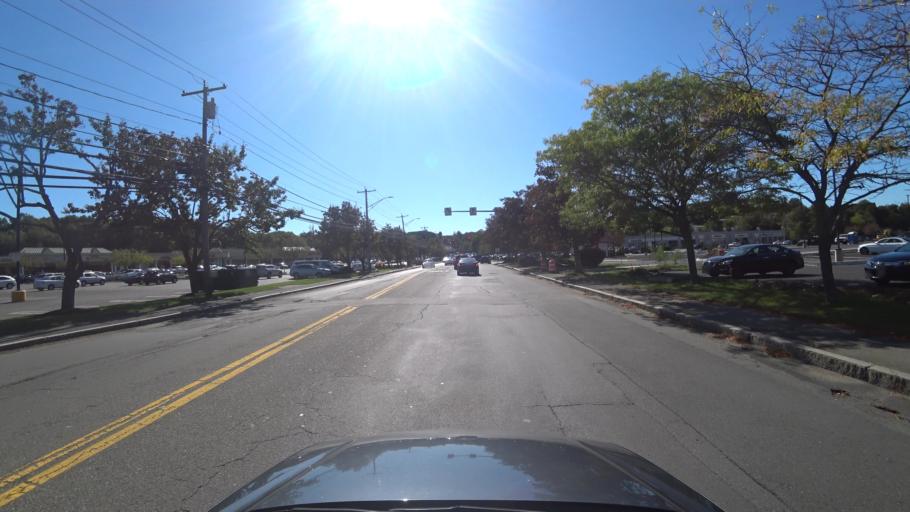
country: US
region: Massachusetts
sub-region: Essex County
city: Swampscott
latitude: 42.4823
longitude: -70.9018
